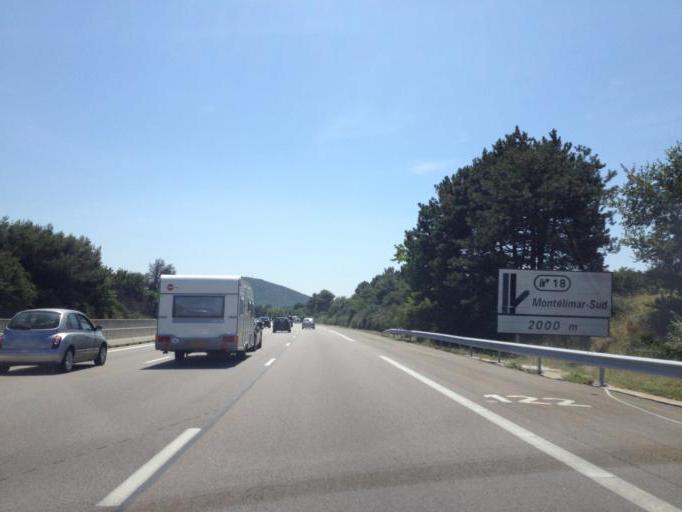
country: FR
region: Rhone-Alpes
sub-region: Departement de la Drome
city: Allan
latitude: 44.5046
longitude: 4.7703
